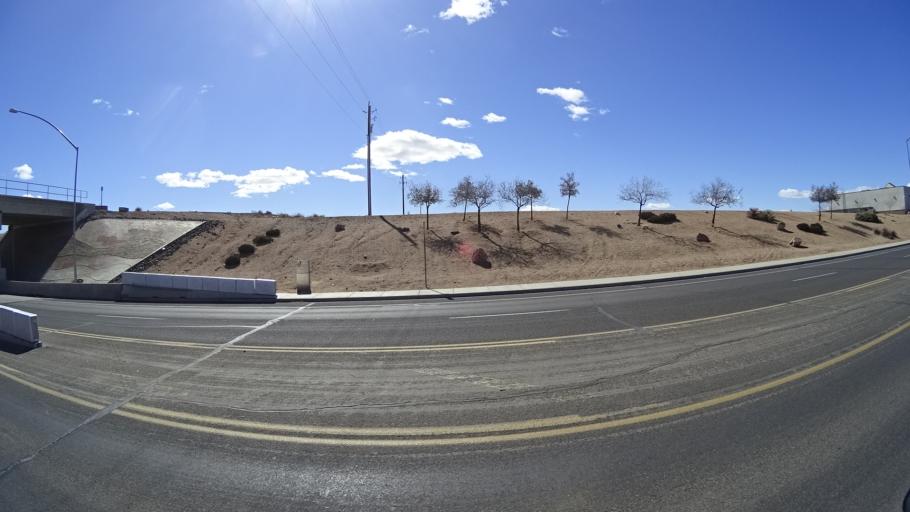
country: US
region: Arizona
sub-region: Mohave County
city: New Kingman-Butler
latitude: 35.2233
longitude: -114.0018
